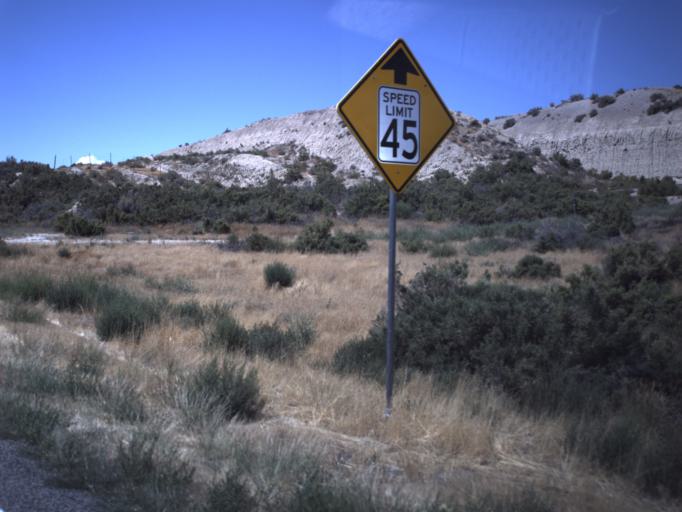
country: US
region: Utah
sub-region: Millard County
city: Delta
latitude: 39.5271
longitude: -112.3544
